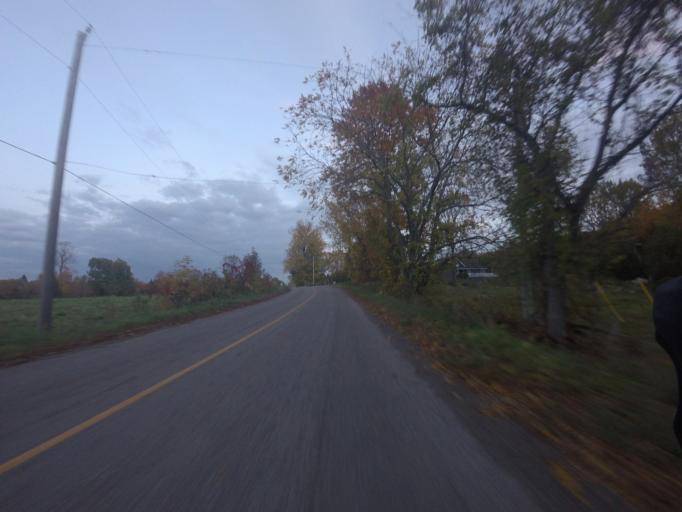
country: CA
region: Ontario
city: Renfrew
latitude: 45.3492
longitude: -76.9450
